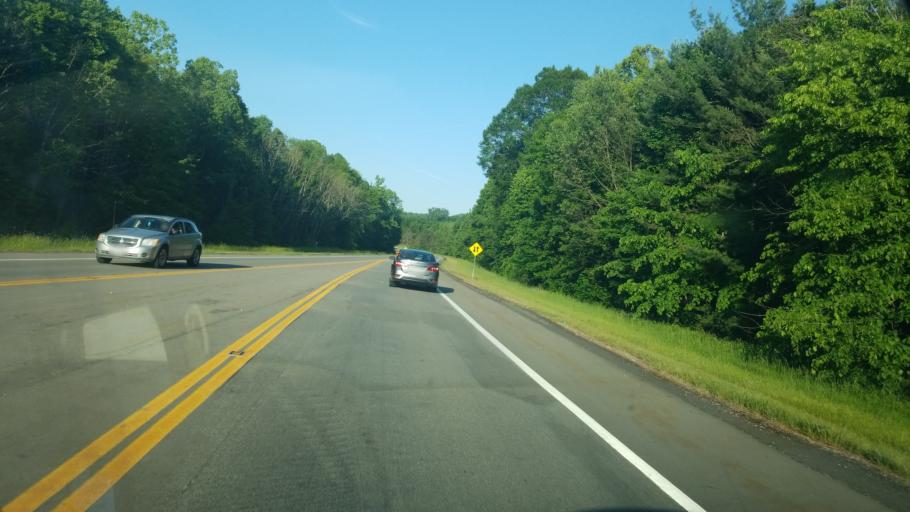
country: US
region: Ohio
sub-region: Portage County
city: Kent
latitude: 41.1345
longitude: -81.3308
